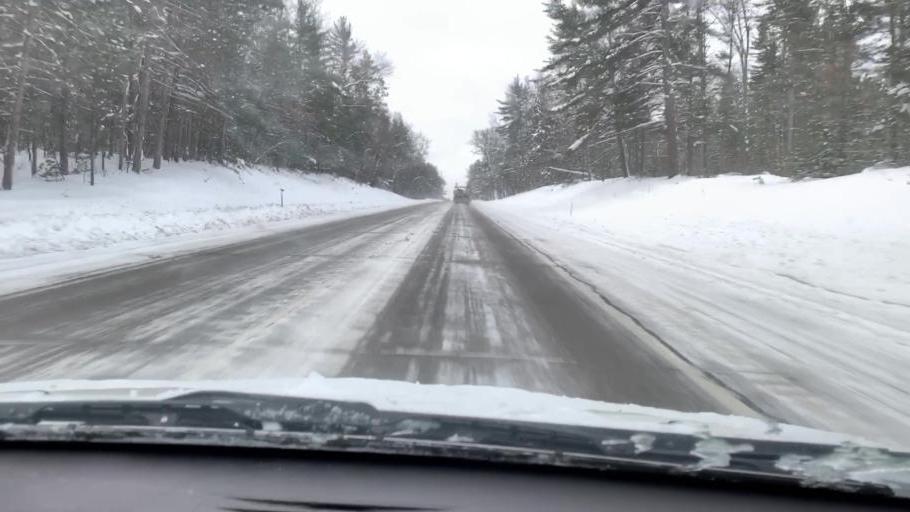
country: US
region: Michigan
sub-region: Wexford County
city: Manton
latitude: 44.5593
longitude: -85.3678
